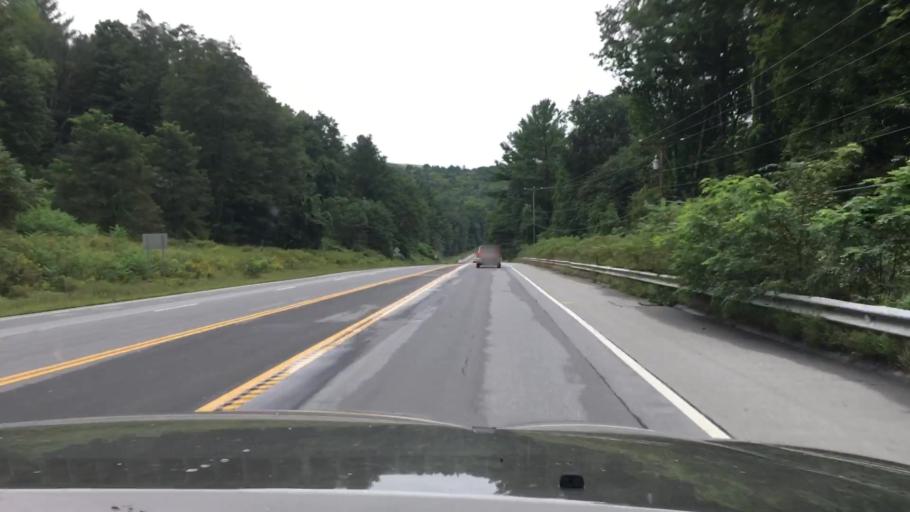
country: US
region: New Hampshire
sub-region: Cheshire County
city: Chesterfield
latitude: 42.8943
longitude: -72.5244
